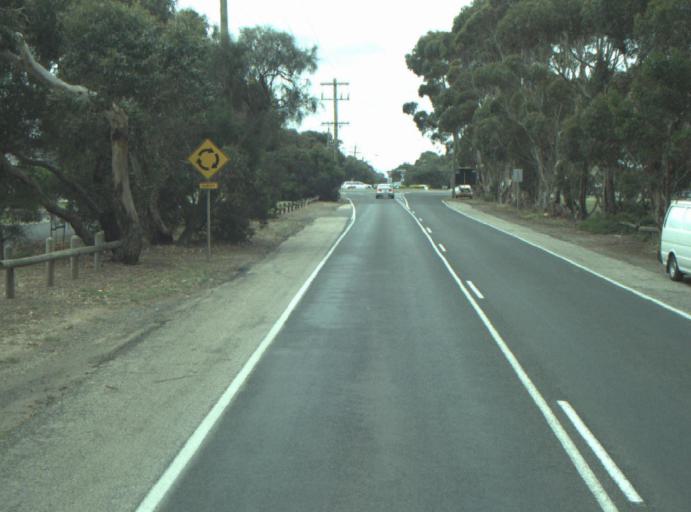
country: AU
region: Victoria
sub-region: Greater Geelong
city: Leopold
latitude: -38.2590
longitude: 144.5353
